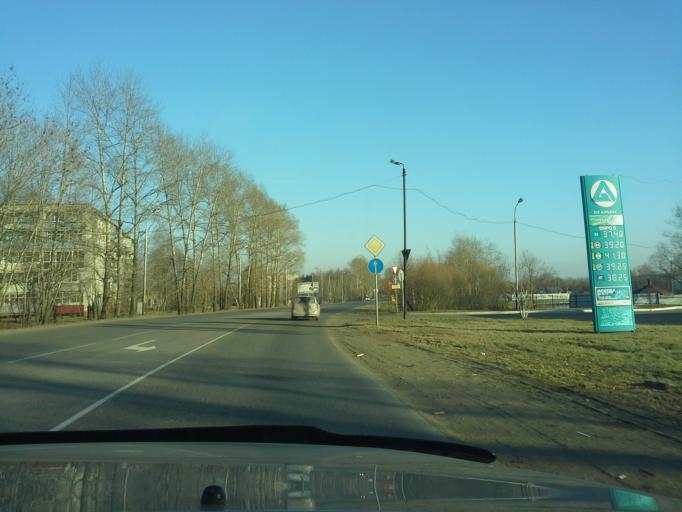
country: RU
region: Khabarovsk Krai
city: Topolevo
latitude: 48.4801
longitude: 135.1480
